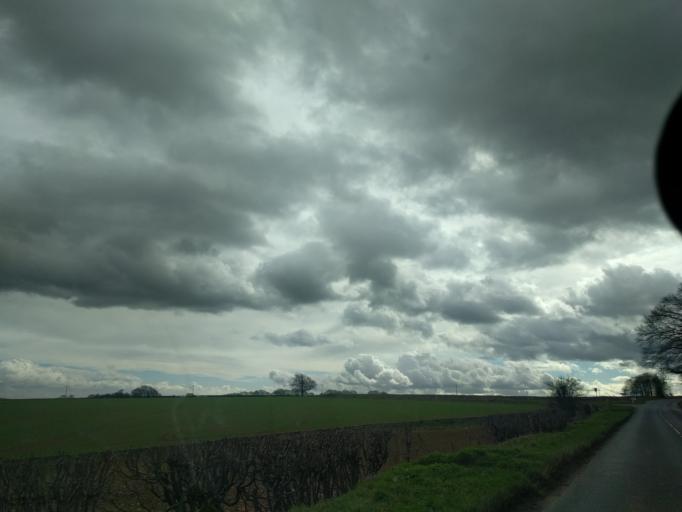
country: GB
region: England
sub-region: Gloucestershire
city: Nailsworth
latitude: 51.6726
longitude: -2.2795
